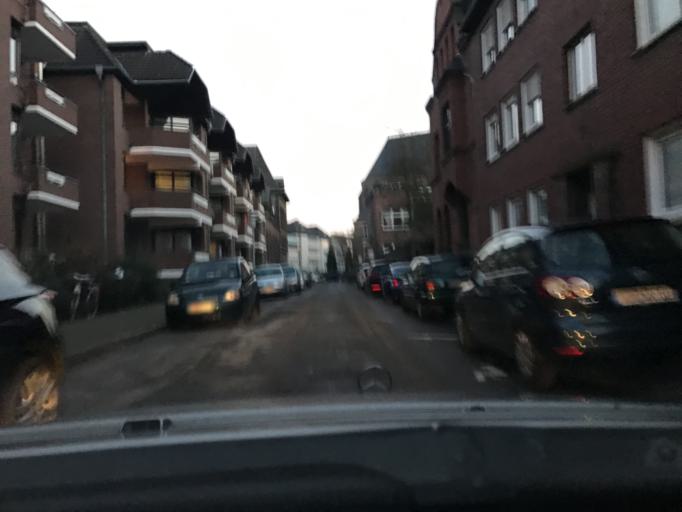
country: DE
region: North Rhine-Westphalia
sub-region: Regierungsbezirk Dusseldorf
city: Krefeld
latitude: 51.3386
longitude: 6.5561
